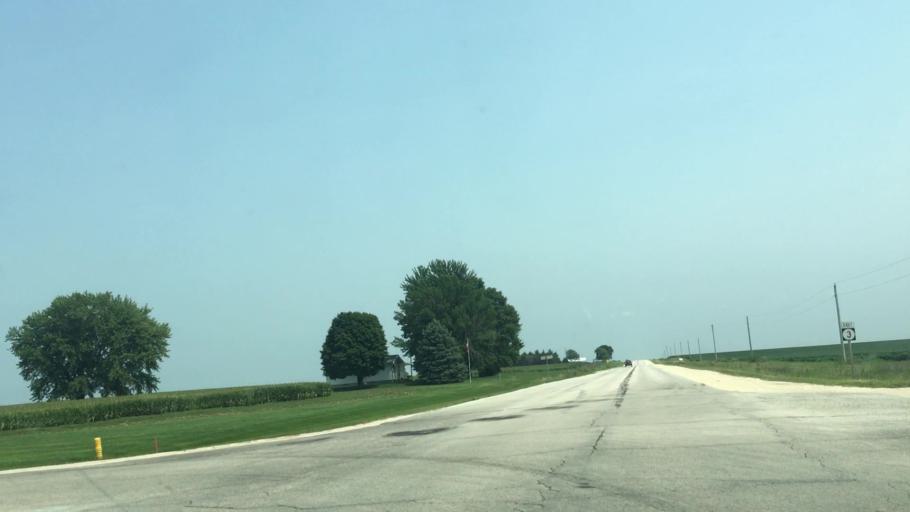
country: US
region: Iowa
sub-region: Fayette County
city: Oelwein
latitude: 42.6873
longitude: -91.8053
